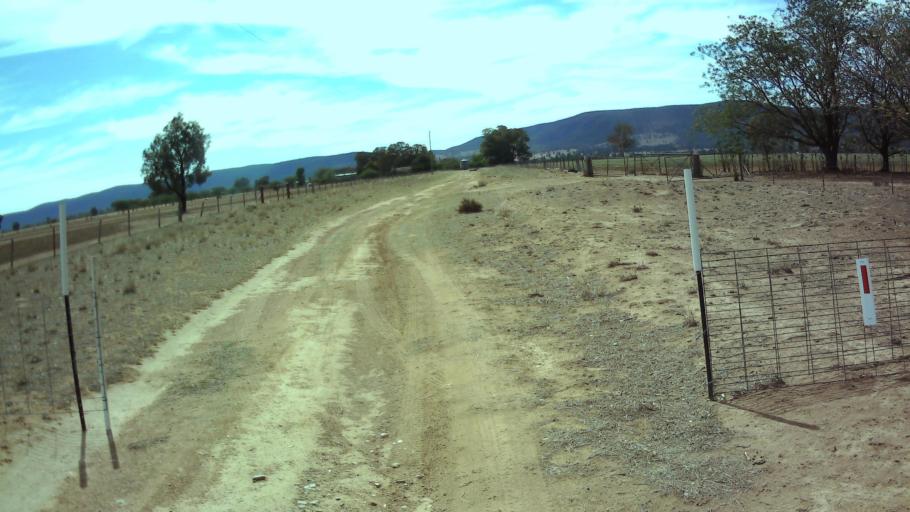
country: AU
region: New South Wales
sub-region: Weddin
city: Grenfell
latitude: -33.7221
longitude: 148.2696
